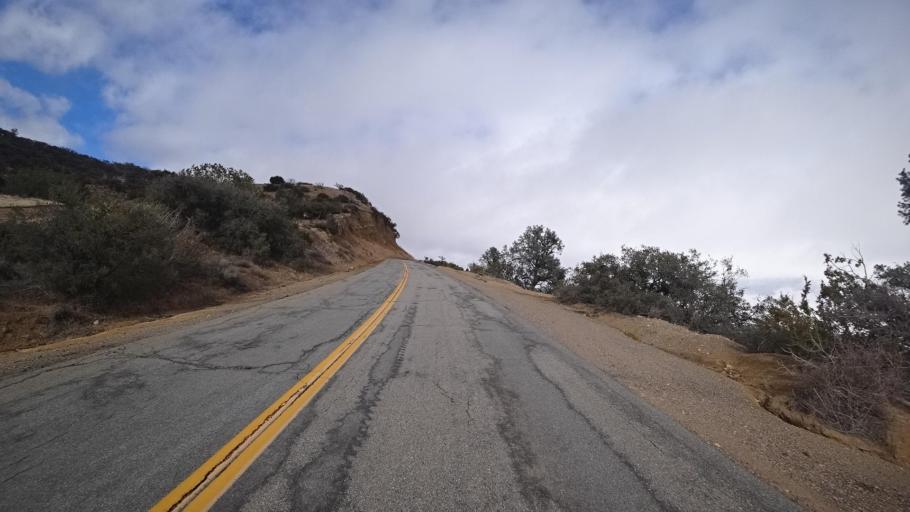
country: US
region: California
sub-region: Kern County
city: Maricopa
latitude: 34.8922
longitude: -119.3569
